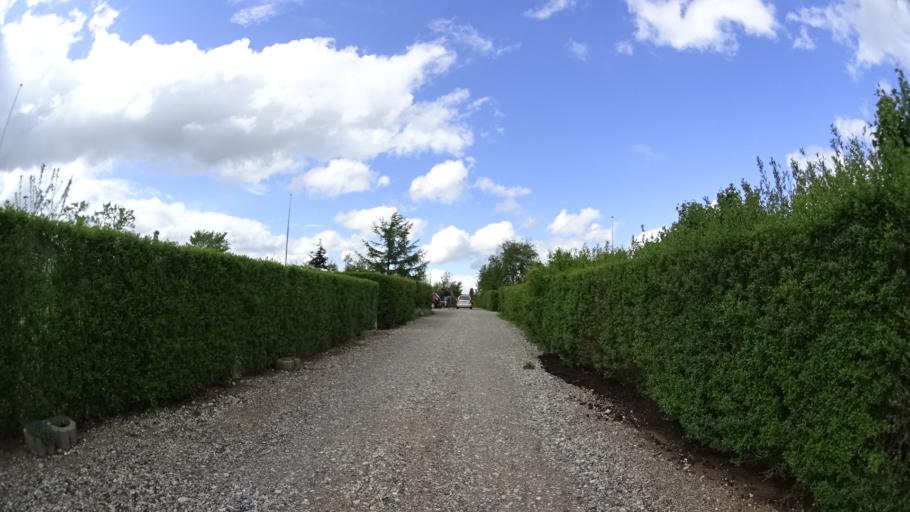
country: DK
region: Central Jutland
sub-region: Arhus Kommune
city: Stavtrup
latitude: 56.1369
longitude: 10.1432
